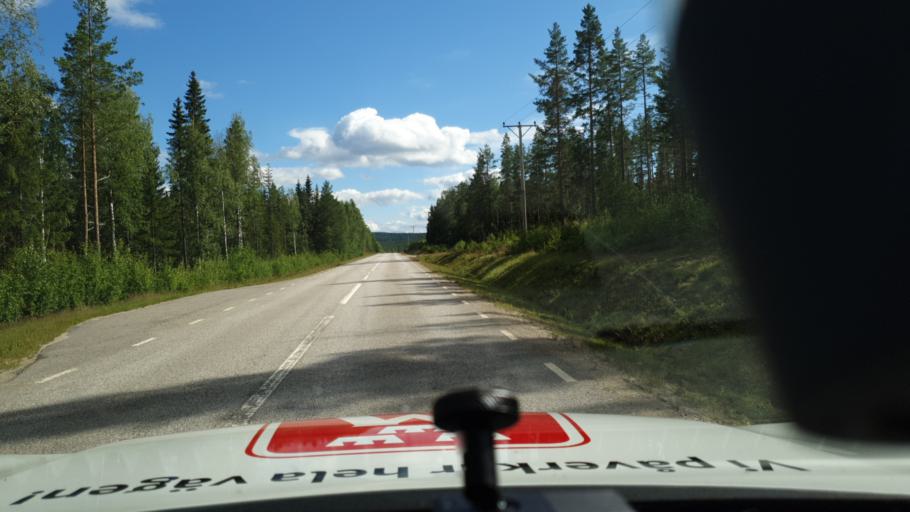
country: NO
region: Hedmark
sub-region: Trysil
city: Innbygda
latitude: 61.0029
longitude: 12.4855
